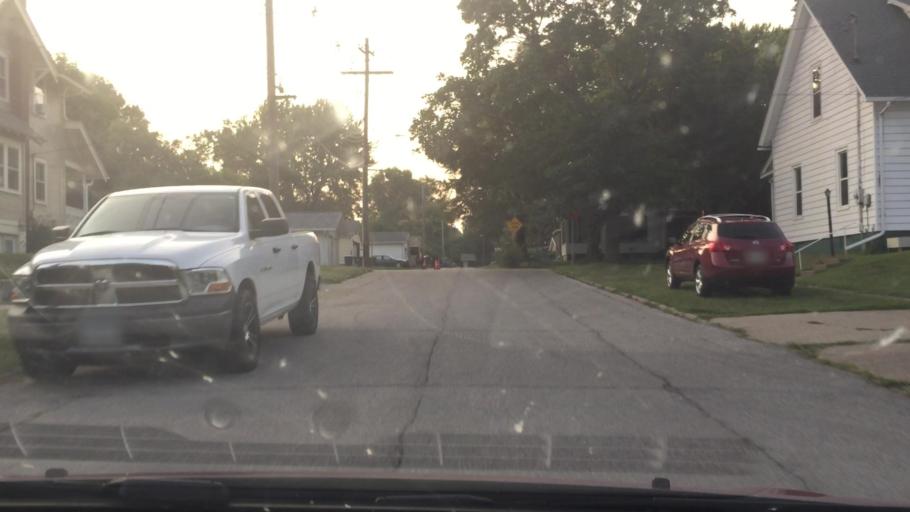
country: US
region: Iowa
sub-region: Muscatine County
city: Muscatine
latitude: 41.4349
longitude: -91.0509
